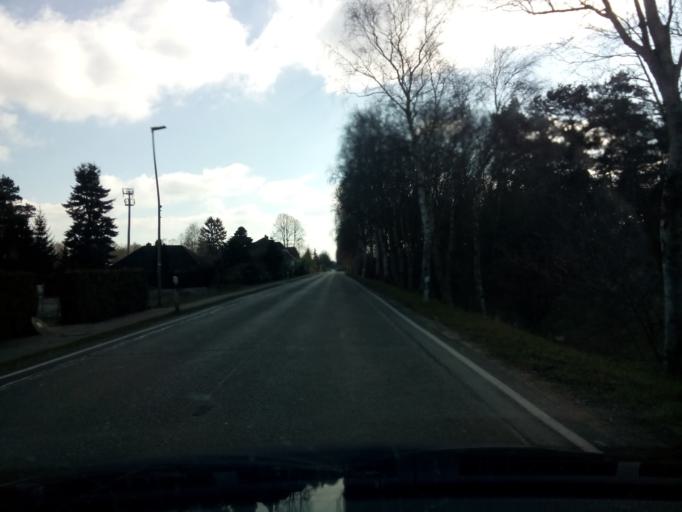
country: DE
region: Lower Saxony
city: Grasberg
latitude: 53.1900
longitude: 8.9798
